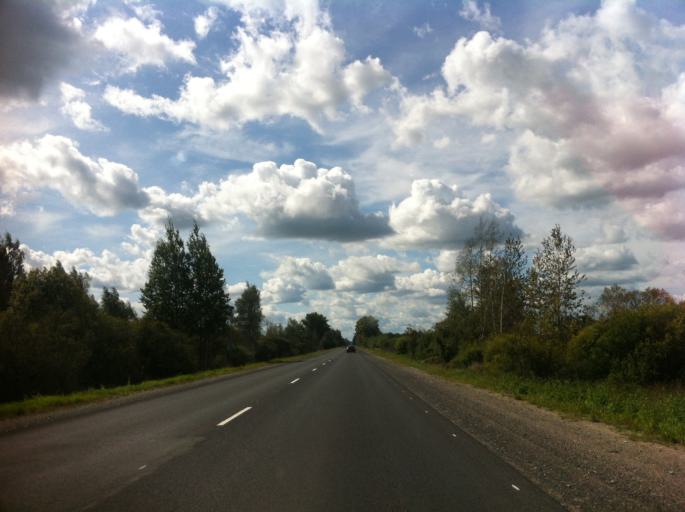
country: RU
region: Pskov
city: Izborsk
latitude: 57.7367
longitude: 27.9962
